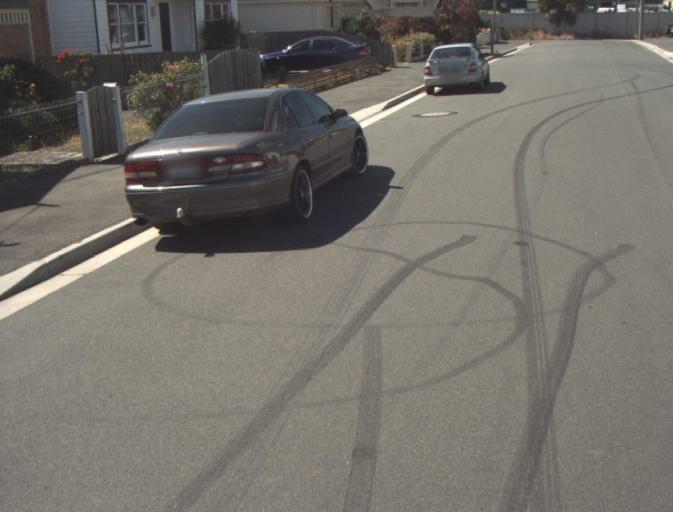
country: AU
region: Tasmania
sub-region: Launceston
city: Launceston
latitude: -41.4173
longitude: 147.1405
